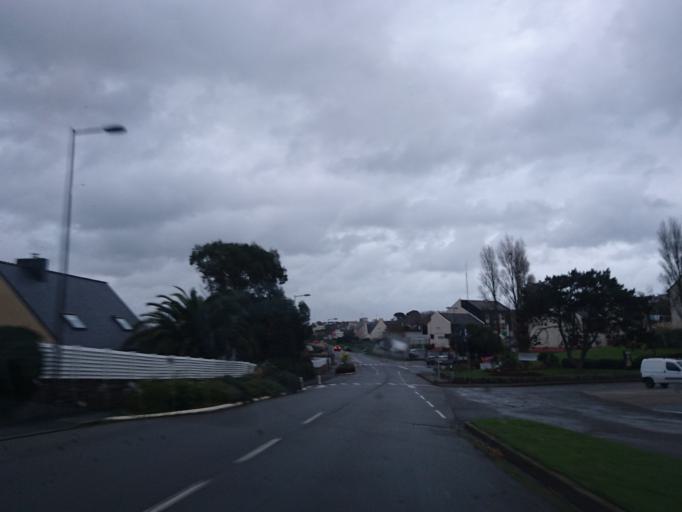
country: FR
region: Brittany
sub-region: Departement du Finistere
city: Le Conquet
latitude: 48.3598
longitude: -4.7646
